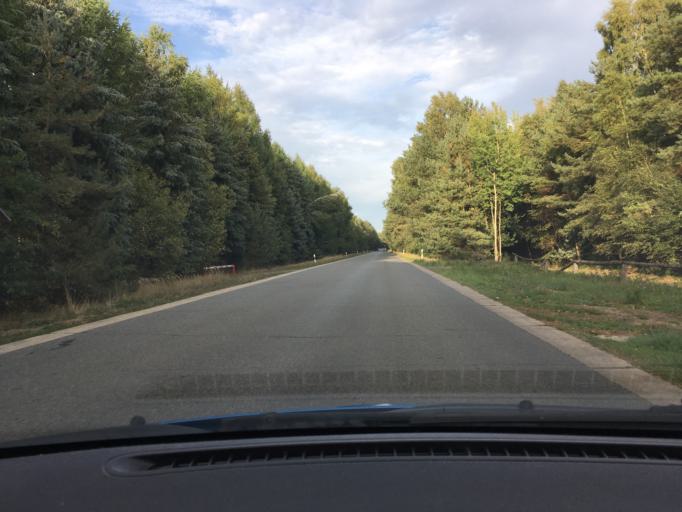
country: DE
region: Lower Saxony
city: Soltau
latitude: 52.9657
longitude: 9.9151
